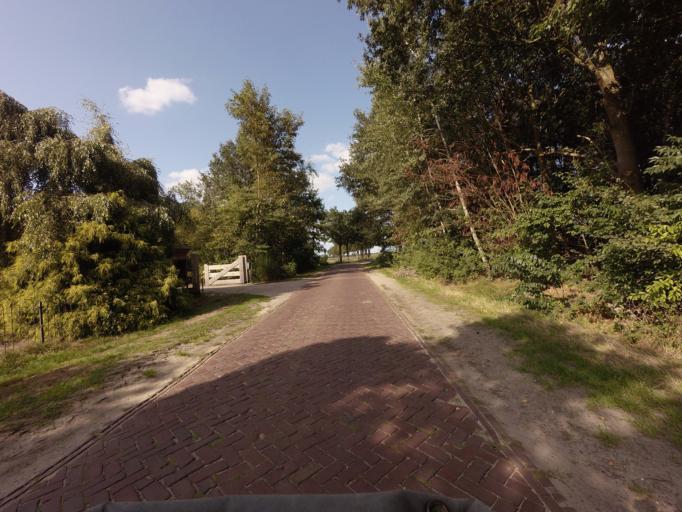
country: NL
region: Drenthe
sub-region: Gemeente Westerveld
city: Dwingeloo
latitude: 52.8348
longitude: 6.3919
